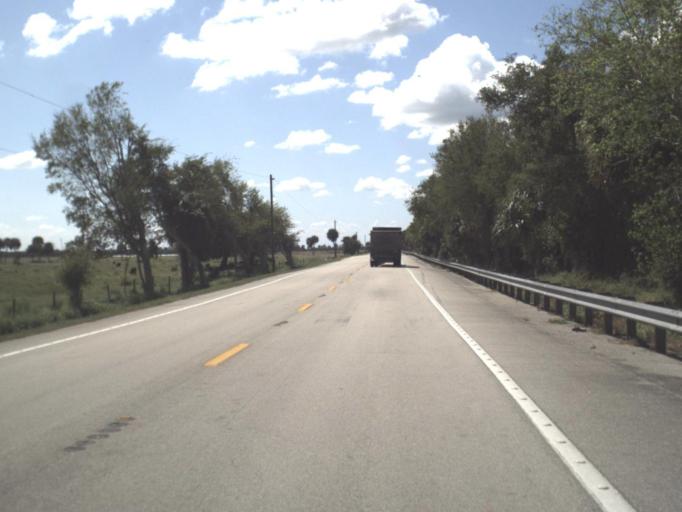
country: US
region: Florida
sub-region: Glades County
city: Buckhead Ridge
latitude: 27.1259
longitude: -80.9112
